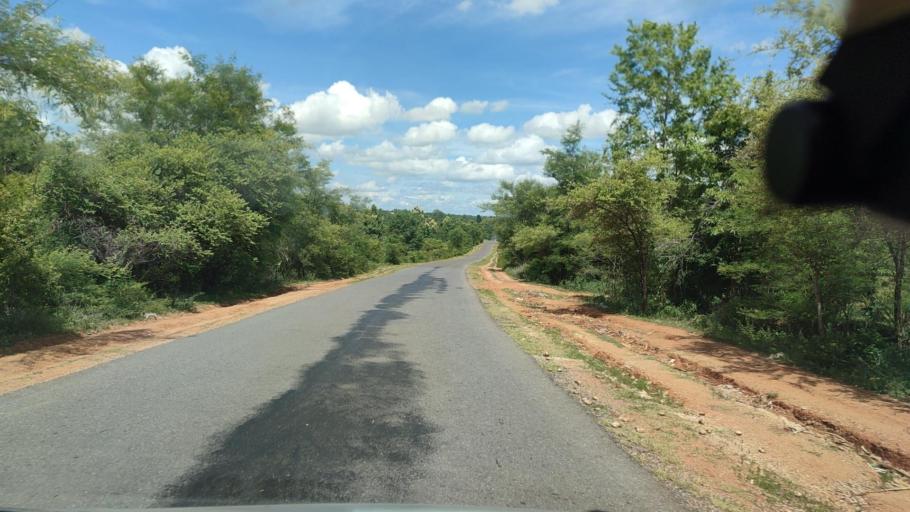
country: MM
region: Magway
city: Magway
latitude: 20.1905
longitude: 95.1845
